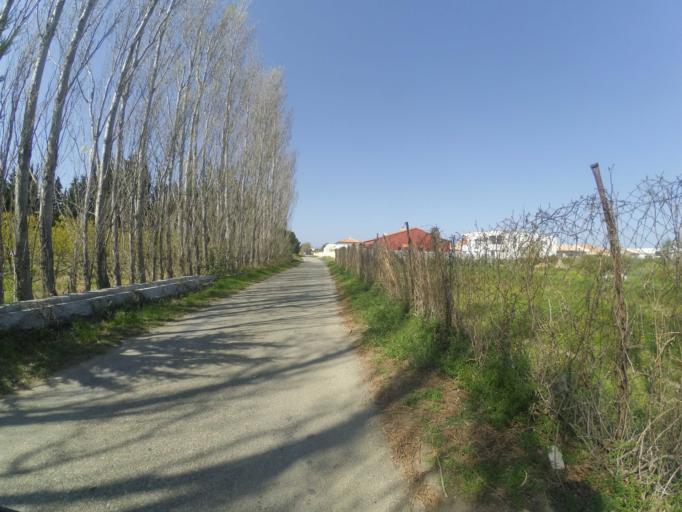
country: FR
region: Languedoc-Roussillon
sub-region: Departement des Pyrenees-Orientales
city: Corneilla-la-Riviere
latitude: 42.6772
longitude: 2.7493
